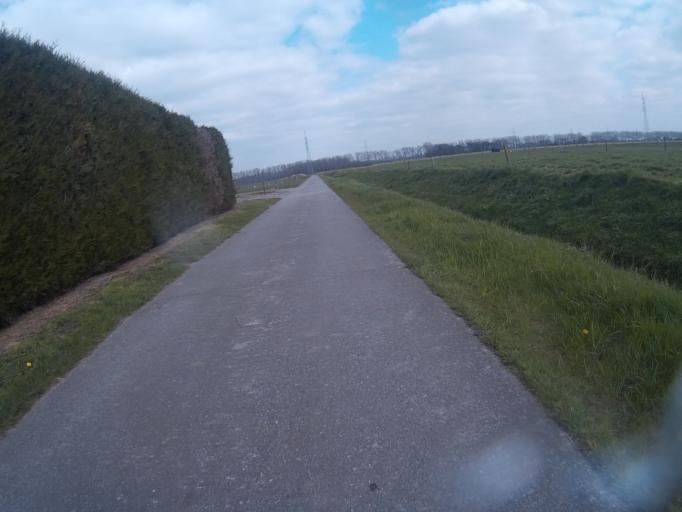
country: BE
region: Flanders
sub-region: Provincie Oost-Vlaanderen
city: Zomergem
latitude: 51.1488
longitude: 3.5402
